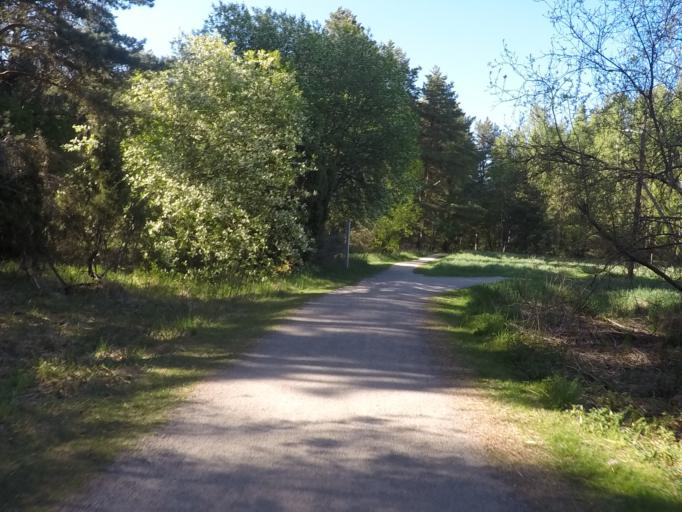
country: SE
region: Soedermanland
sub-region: Eskilstuna Kommun
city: Eskilstuna
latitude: 59.3887
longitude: 16.5267
